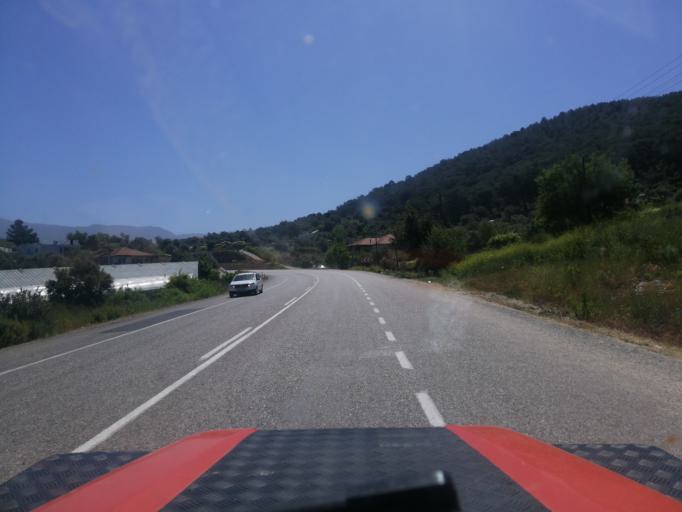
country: TR
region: Antalya
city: Kalkan
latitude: 36.2925
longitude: 29.3369
